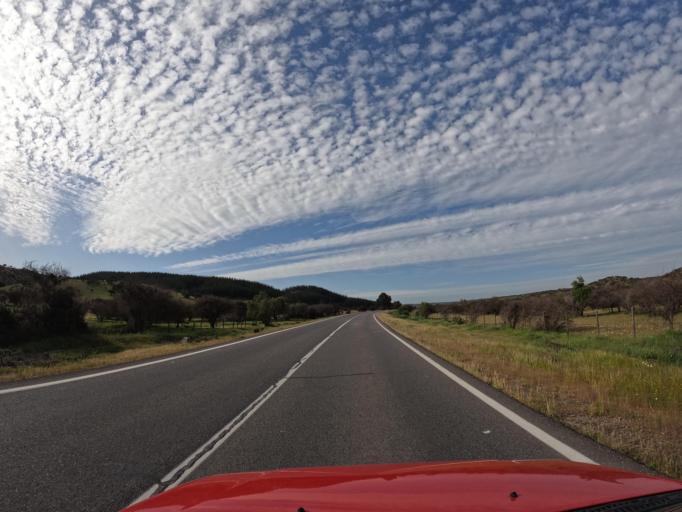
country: CL
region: O'Higgins
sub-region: Provincia de Colchagua
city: Santa Cruz
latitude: -34.3068
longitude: -71.7368
